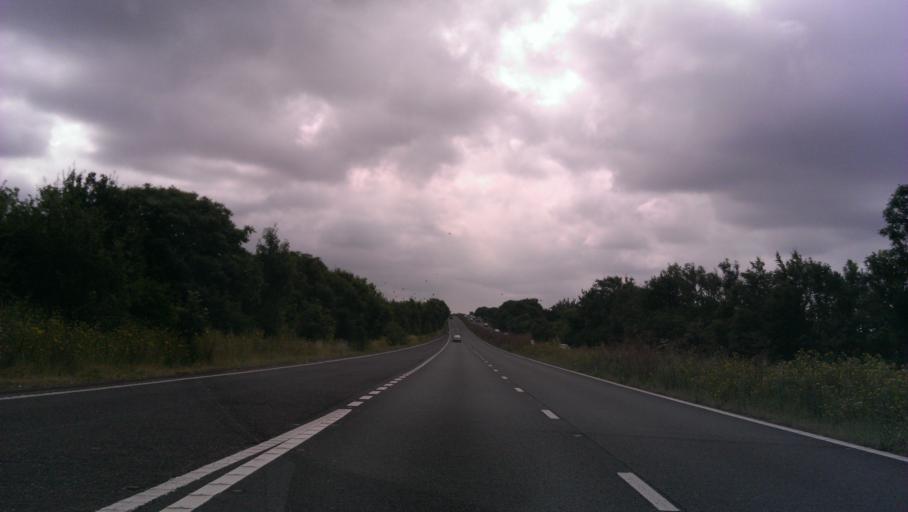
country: GB
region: England
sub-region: Kent
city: Barham
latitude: 51.2332
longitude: 1.1414
